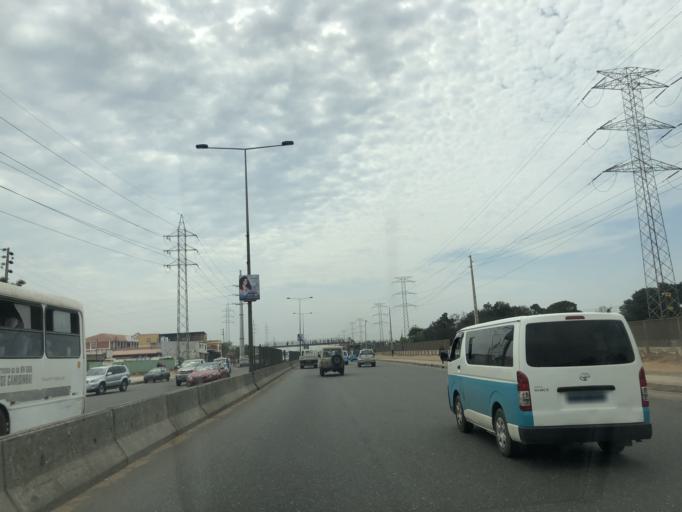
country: AO
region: Luanda
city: Luanda
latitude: -8.8663
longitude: 13.3129
